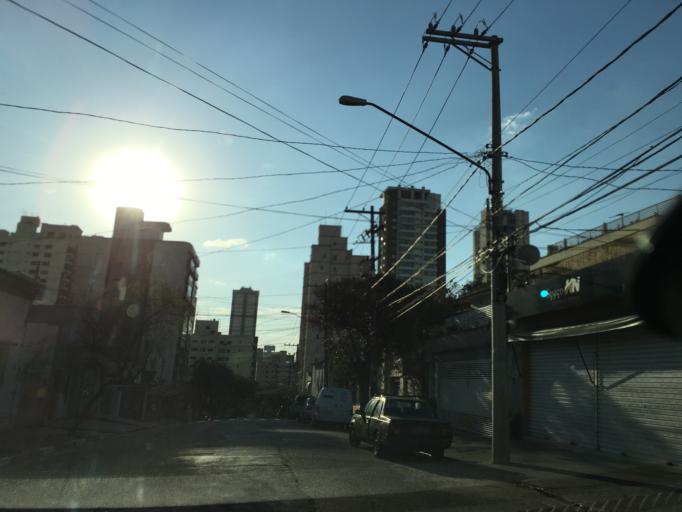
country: BR
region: Sao Paulo
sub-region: Sao Paulo
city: Sao Paulo
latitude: -23.4938
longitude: -46.6362
